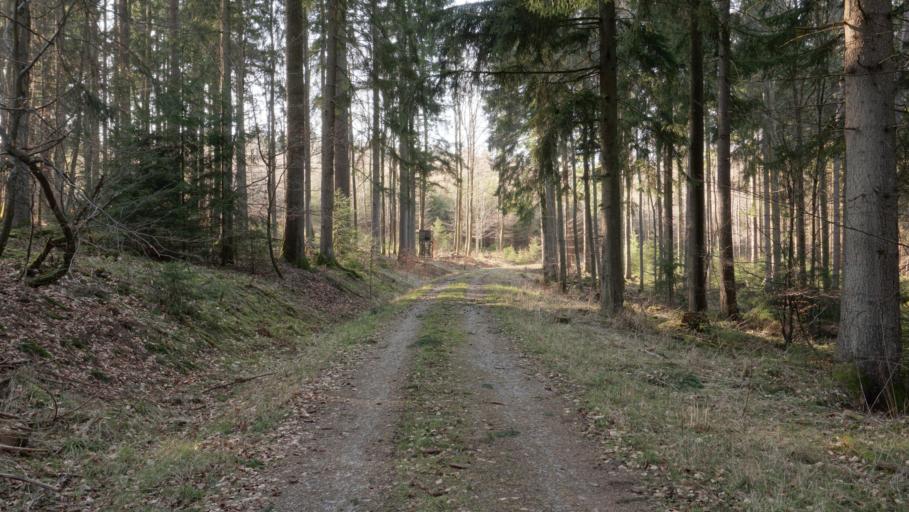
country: DE
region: Baden-Wuerttemberg
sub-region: Karlsruhe Region
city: Fahrenbach
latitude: 49.4525
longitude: 9.1421
